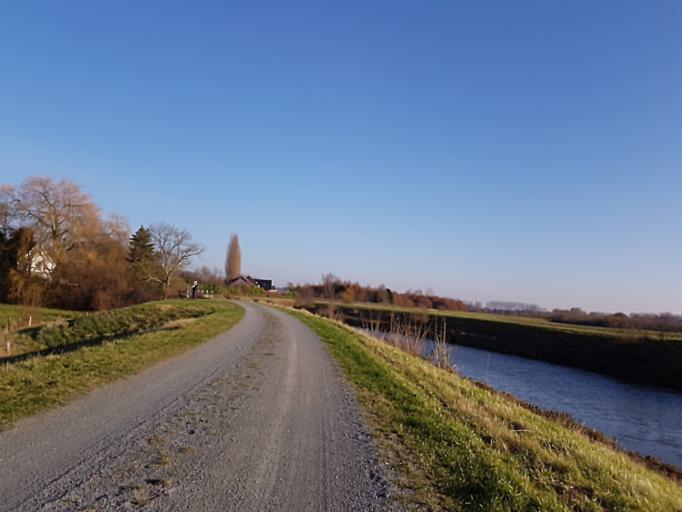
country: BE
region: Flanders
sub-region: Provincie Antwerpen
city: Bonheiden
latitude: 51.0088
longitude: 4.5267
